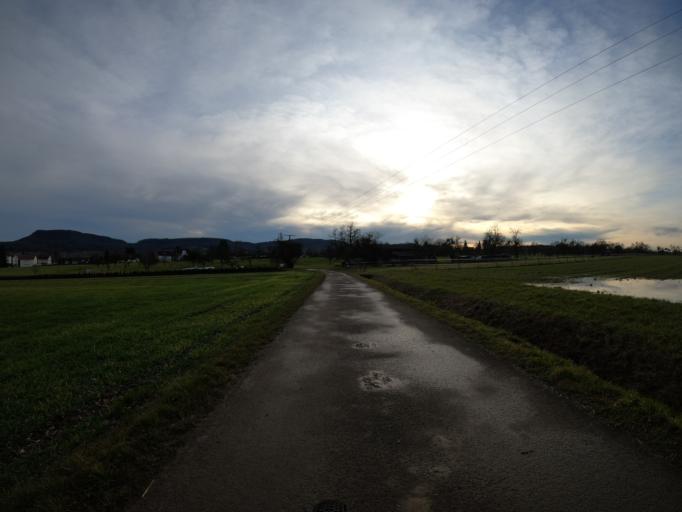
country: DE
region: Baden-Wuerttemberg
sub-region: Regierungsbezirk Stuttgart
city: Heiningen
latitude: 48.6687
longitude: 9.6487
